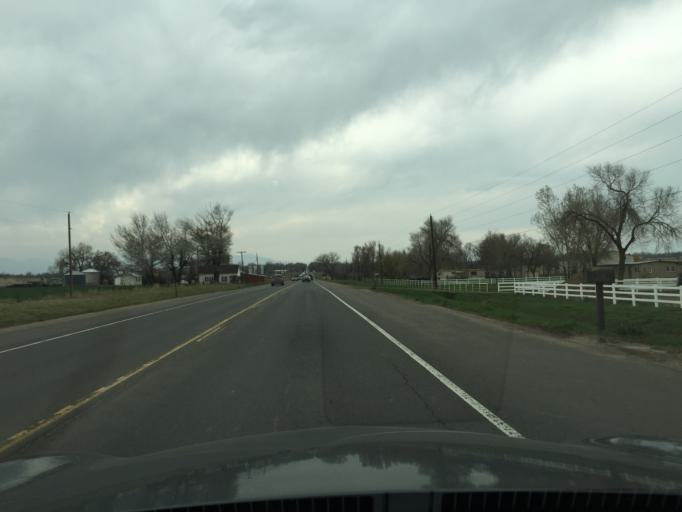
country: US
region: Colorado
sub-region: Boulder County
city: Lafayette
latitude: 40.0003
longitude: -105.0680
